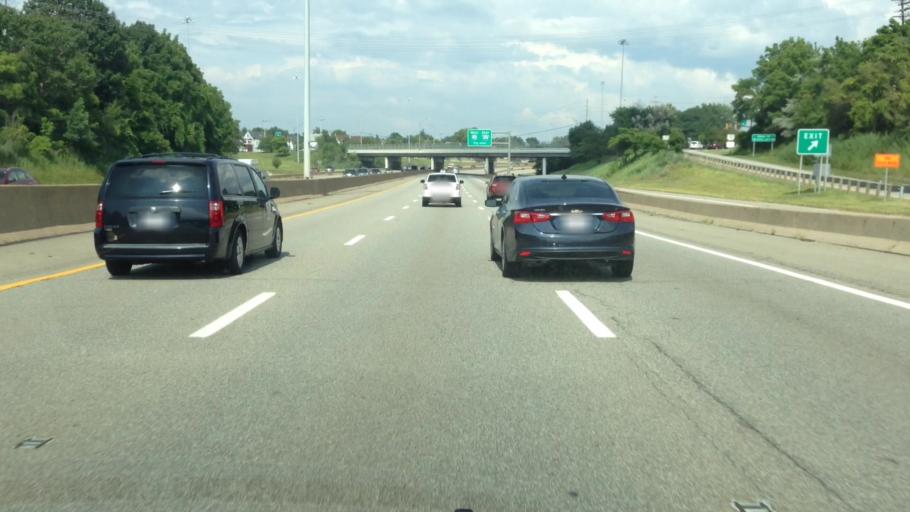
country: US
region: Ohio
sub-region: Cuyahoga County
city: Brooklyn
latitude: 41.4540
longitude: -81.7183
